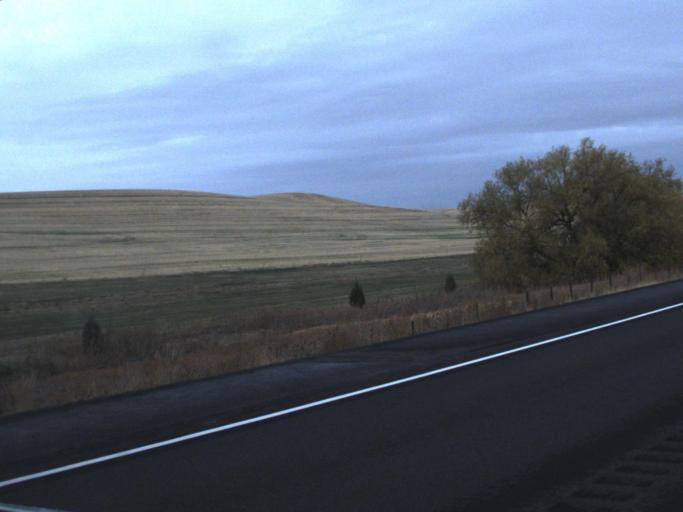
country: US
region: Washington
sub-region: Whitman County
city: Pullman
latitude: 46.7304
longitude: -117.2237
